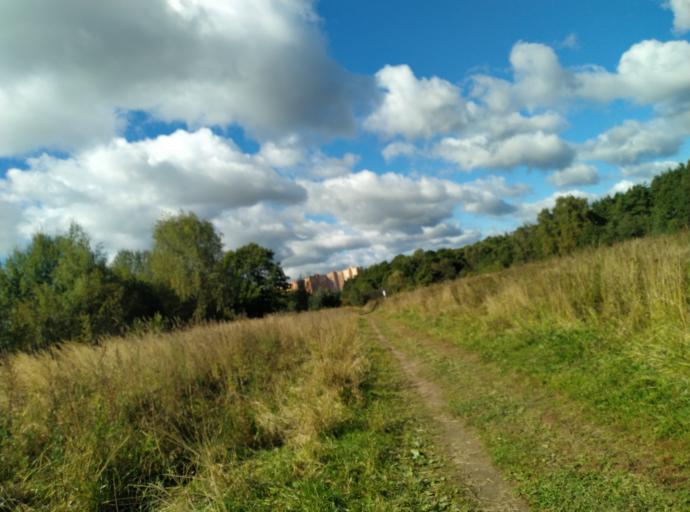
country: RU
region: Moscow
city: Khimki
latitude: 55.8631
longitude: 37.4129
